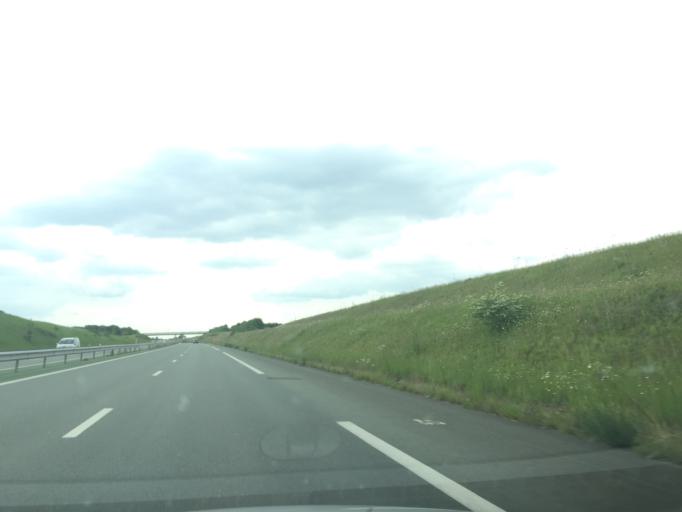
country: FR
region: Poitou-Charentes
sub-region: Departement des Deux-Sevres
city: Villiers-en-Plaine
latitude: 46.4222
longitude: -0.5514
